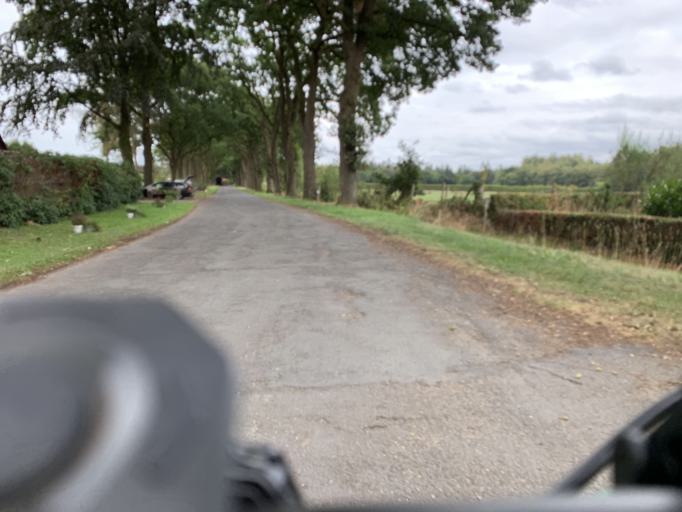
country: DE
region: Lower Saxony
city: Westerstede
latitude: 53.2338
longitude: 7.9428
